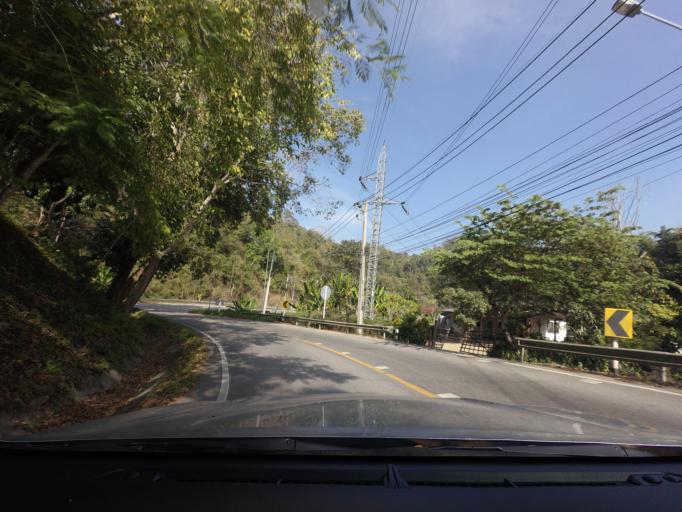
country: TH
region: Mae Hong Son
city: Mae Hi
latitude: 19.2049
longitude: 98.6757
